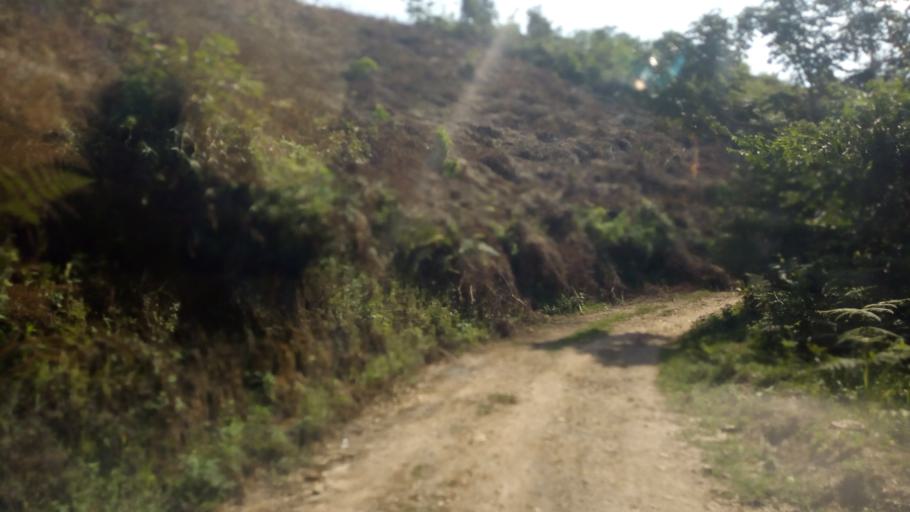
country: UG
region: Western Region
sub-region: Kisoro District
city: Kisoro
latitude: -1.0952
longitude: 29.5851
